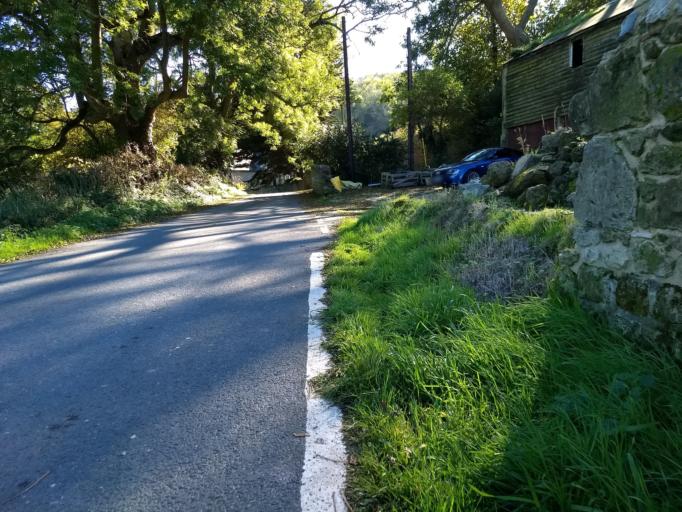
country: GB
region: England
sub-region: Isle of Wight
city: Ventnor
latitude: 50.6014
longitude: -1.2283
